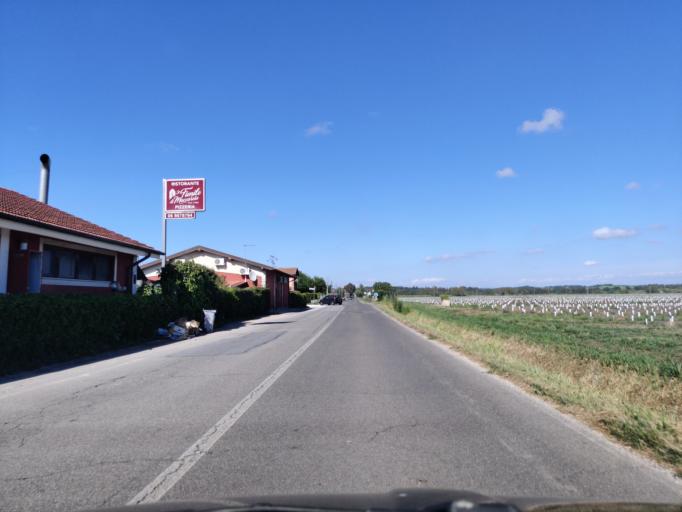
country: IT
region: Latium
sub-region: Citta metropolitana di Roma Capitale
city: Maccarese
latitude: 41.8812
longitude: 12.2158
